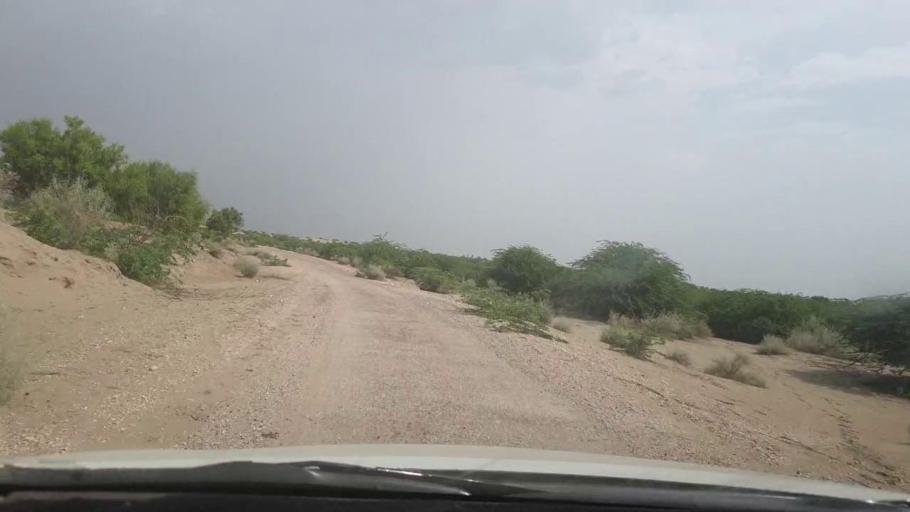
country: PK
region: Sindh
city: Kot Diji
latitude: 27.3366
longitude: 69.0455
